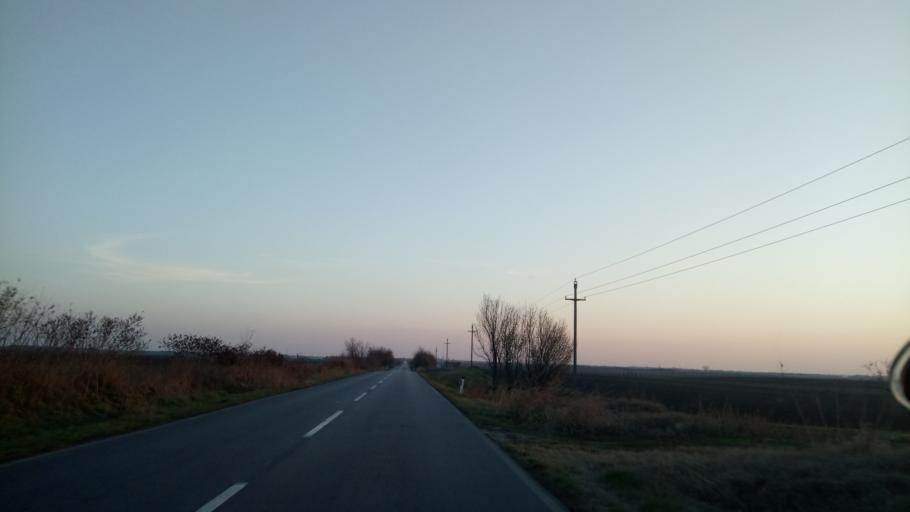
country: RS
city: Surduk
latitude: 45.0500
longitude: 20.3320
